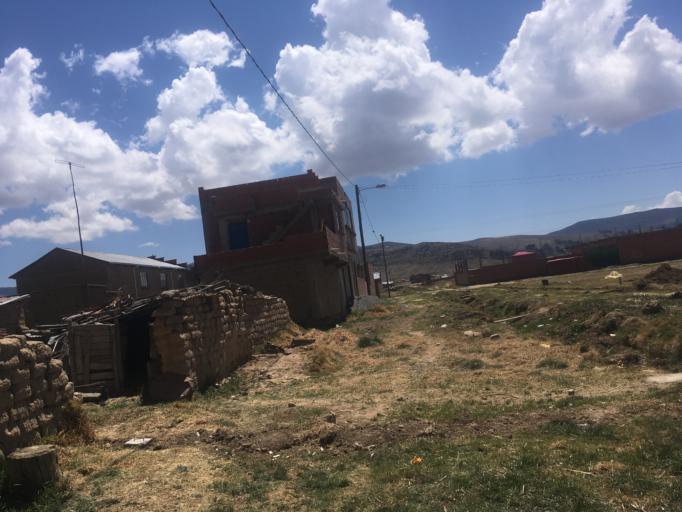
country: BO
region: La Paz
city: Huatajata
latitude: -16.1929
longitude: -68.7429
